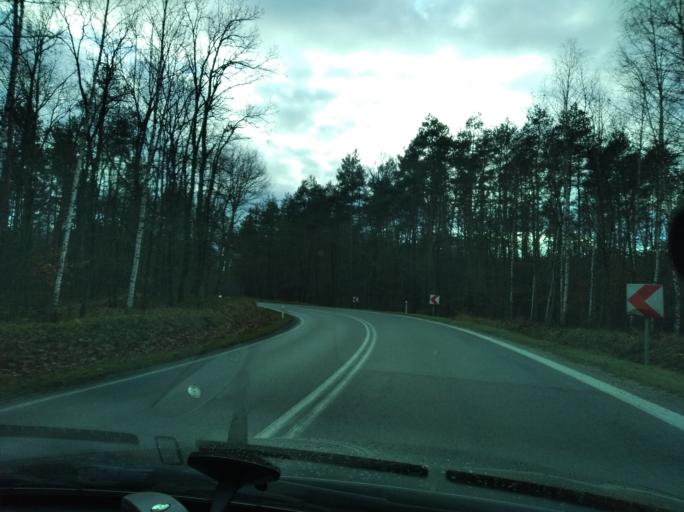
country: PL
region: Subcarpathian Voivodeship
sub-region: Powiat lancucki
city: Rakszawa
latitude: 50.1332
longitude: 22.2339
